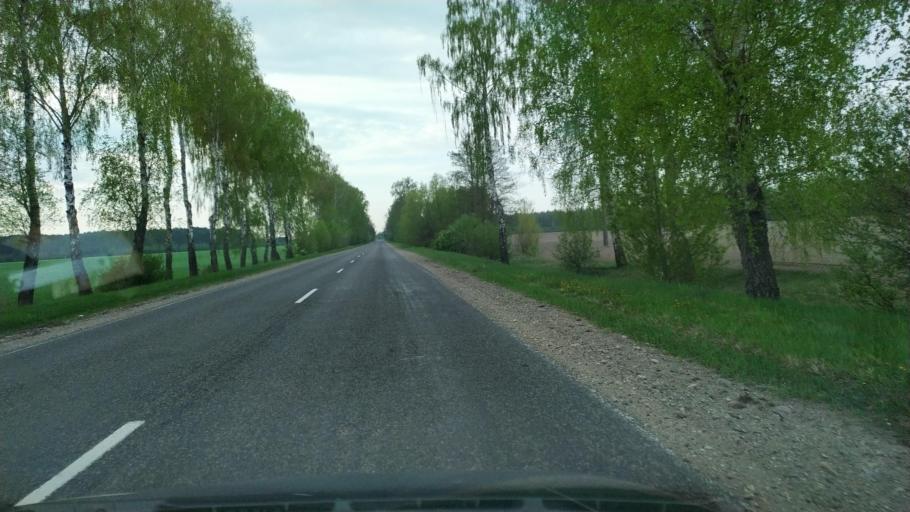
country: BY
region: Brest
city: Zhabinka
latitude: 52.2487
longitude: 23.9713
